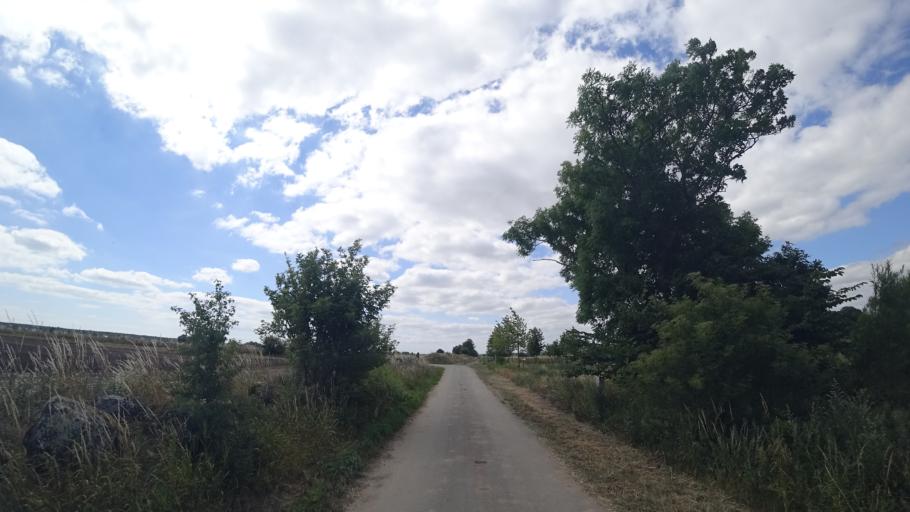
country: SE
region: Skane
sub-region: Kristianstads Kommun
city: Ahus
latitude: 55.9701
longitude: 14.2623
